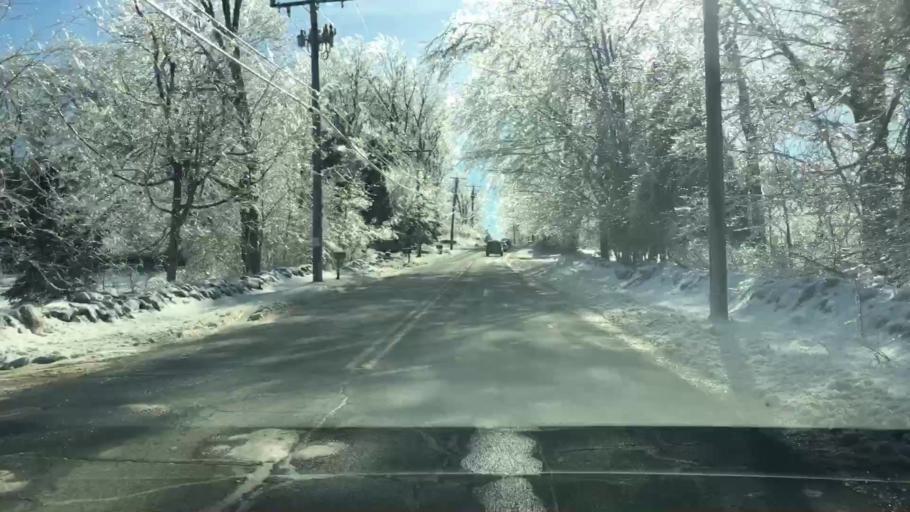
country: US
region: Connecticut
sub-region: Fairfield County
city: Newtown
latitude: 41.3911
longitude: -73.2587
